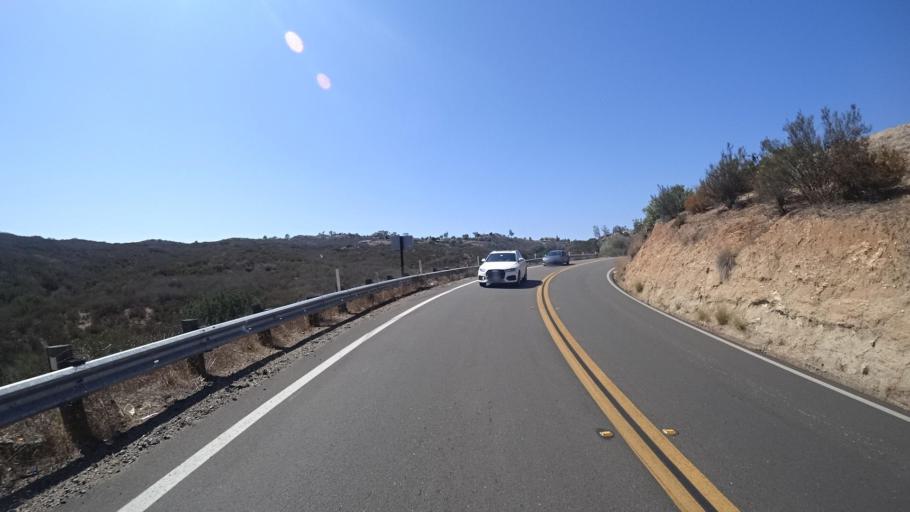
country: US
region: California
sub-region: San Diego County
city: Harbison Canyon
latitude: 32.8265
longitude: -116.8372
